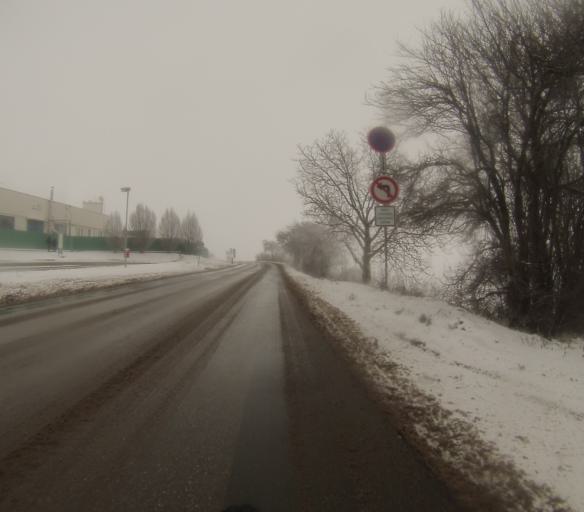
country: CZ
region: South Moravian
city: Strelice
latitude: 49.1585
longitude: 16.5054
